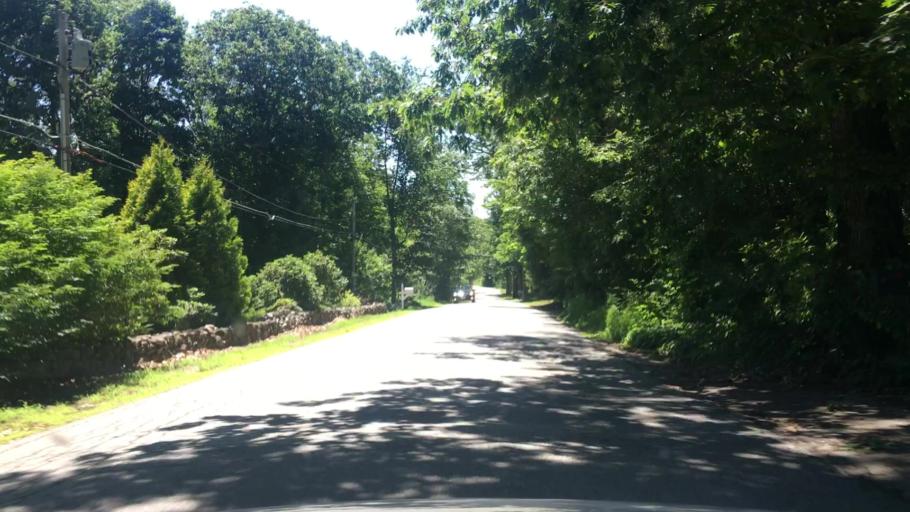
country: US
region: New Hampshire
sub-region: Merrimack County
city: Hopkinton
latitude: 43.2234
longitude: -71.6784
